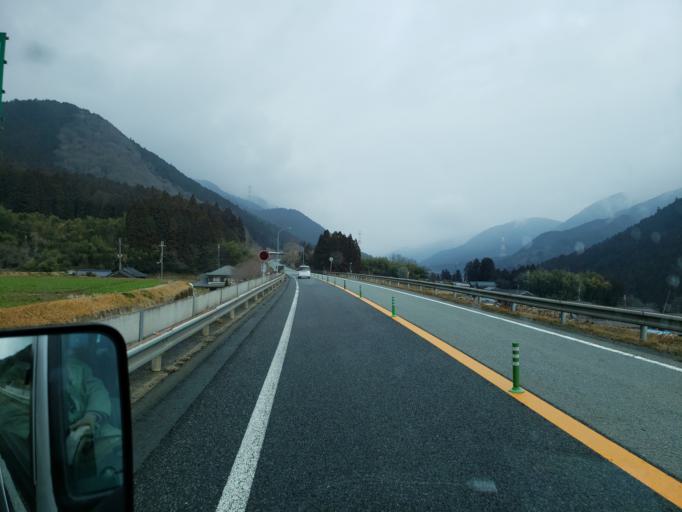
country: JP
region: Hyogo
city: Nishiwaki
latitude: 35.0981
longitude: 134.7767
